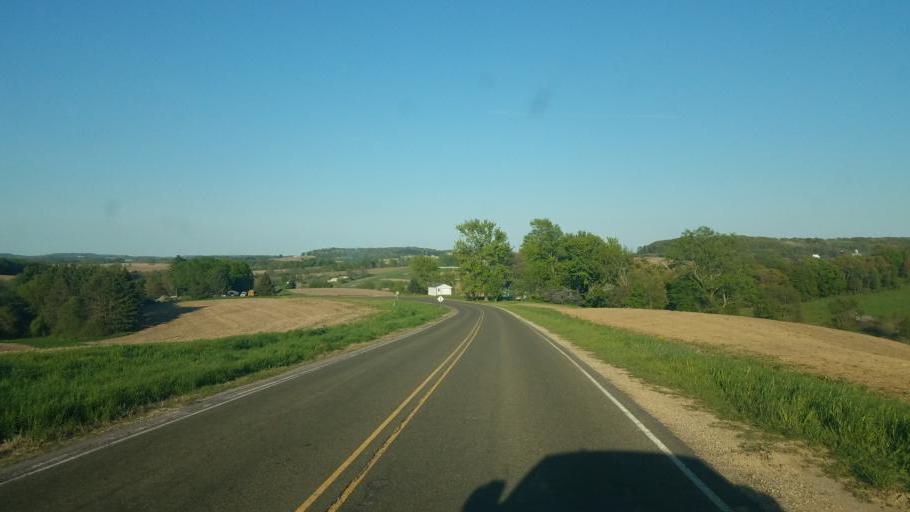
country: US
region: Wisconsin
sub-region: Vernon County
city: Hillsboro
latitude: 43.6513
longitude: -90.3130
